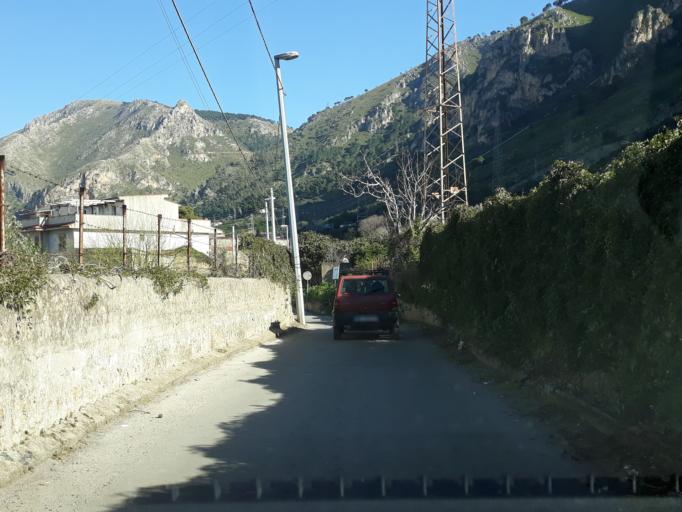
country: IT
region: Sicily
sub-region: Palermo
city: Villa Ciambra
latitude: 38.0756
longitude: 13.3526
